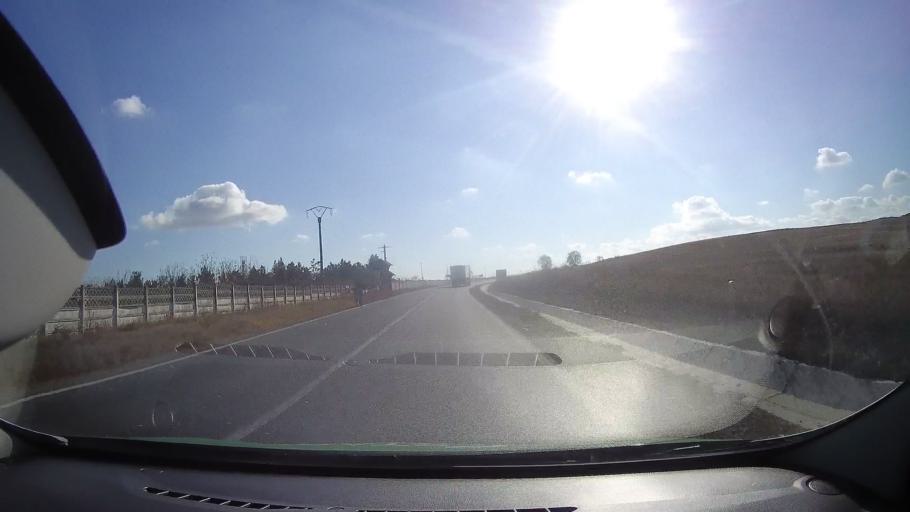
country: RO
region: Tulcea
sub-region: Comuna Baia
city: Baia
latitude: 44.7166
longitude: 28.6814
